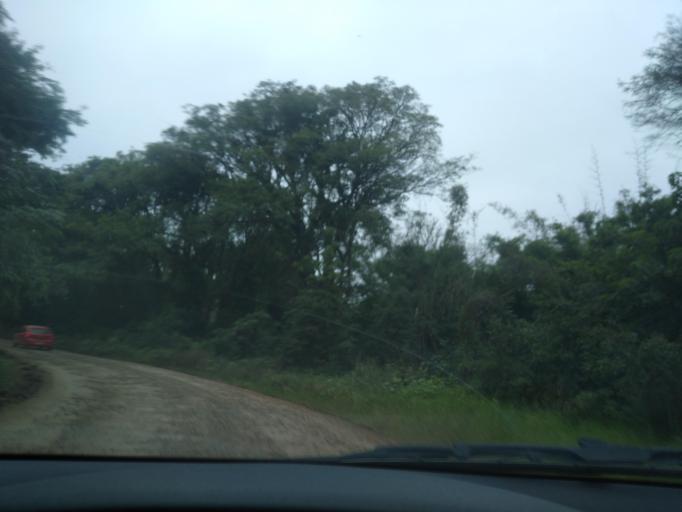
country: AR
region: Chaco
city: Colonia Benitez
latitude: -27.3351
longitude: -58.9658
